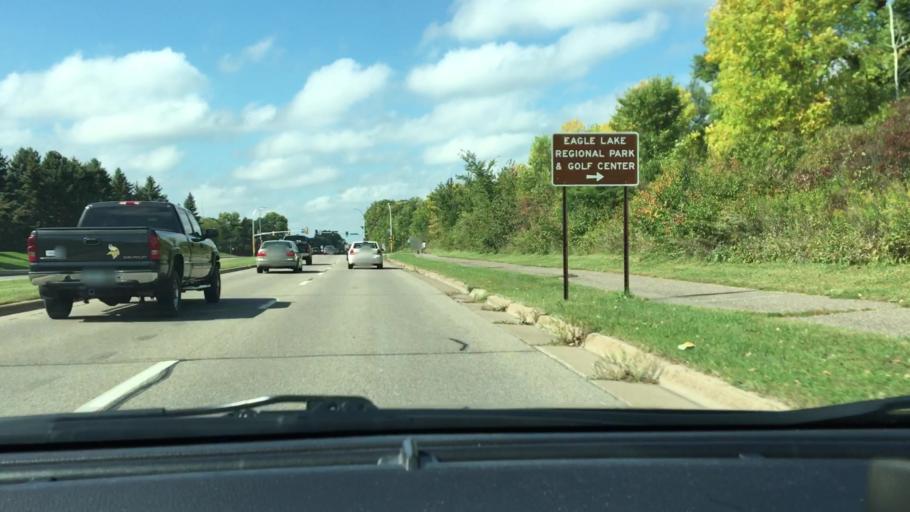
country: US
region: Minnesota
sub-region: Hennepin County
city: New Hope
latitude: 45.0587
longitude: -93.4179
